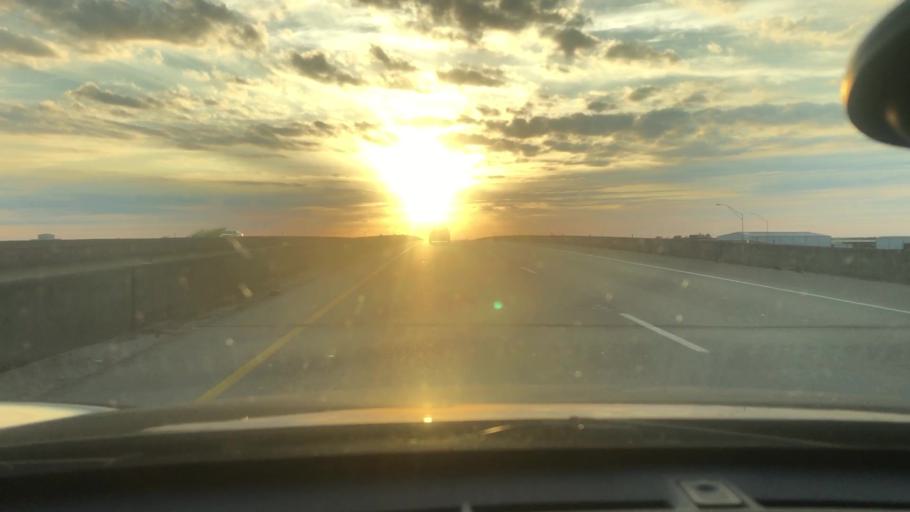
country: US
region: Texas
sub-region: Wharton County
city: El Campo
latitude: 29.1744
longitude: -96.3020
